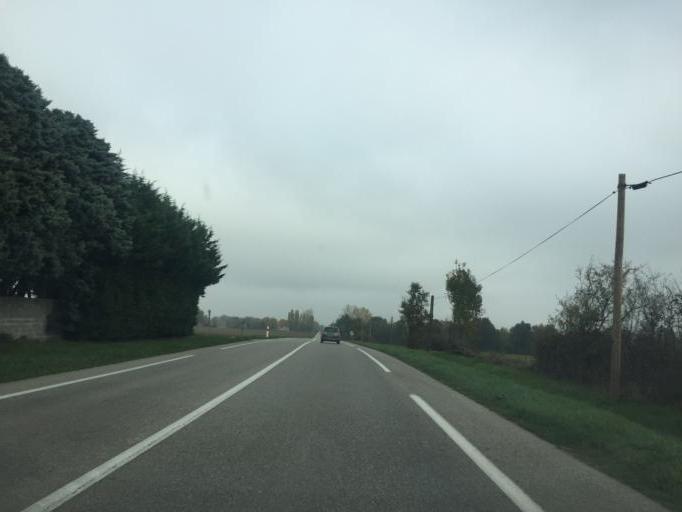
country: FR
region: Rhone-Alpes
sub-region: Departement de l'Ain
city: Saint-Andre-de-Corcy
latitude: 45.9514
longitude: 4.9908
